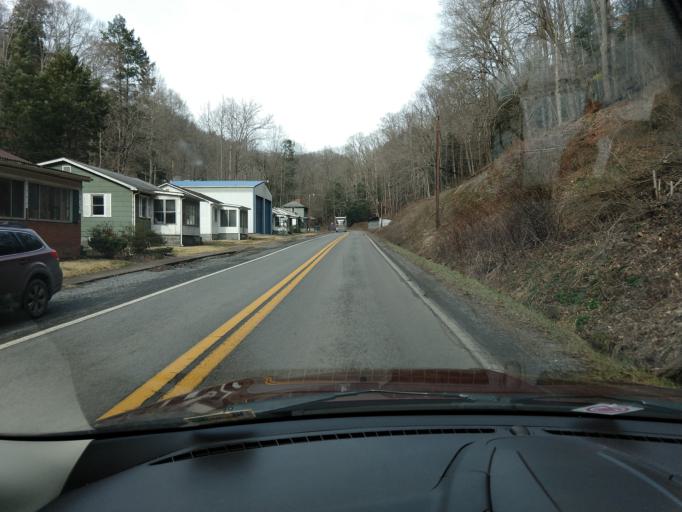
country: US
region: West Virginia
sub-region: McDowell County
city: Welch
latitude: 37.3382
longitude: -81.6722
